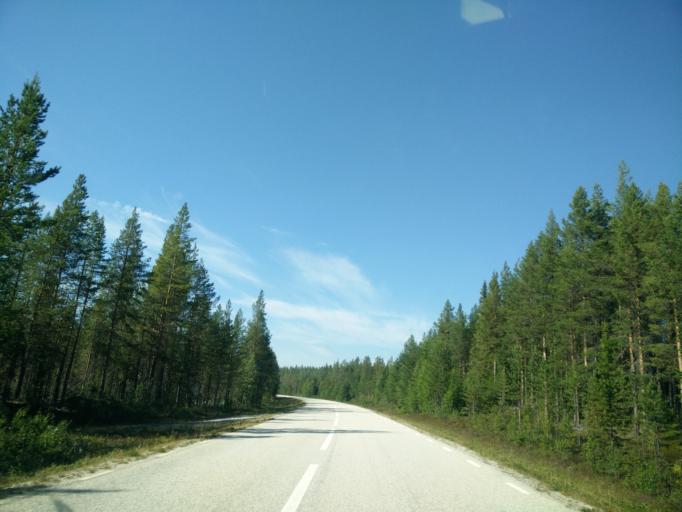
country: SE
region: Jaemtland
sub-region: Are Kommun
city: Jarpen
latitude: 62.8216
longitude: 13.5037
